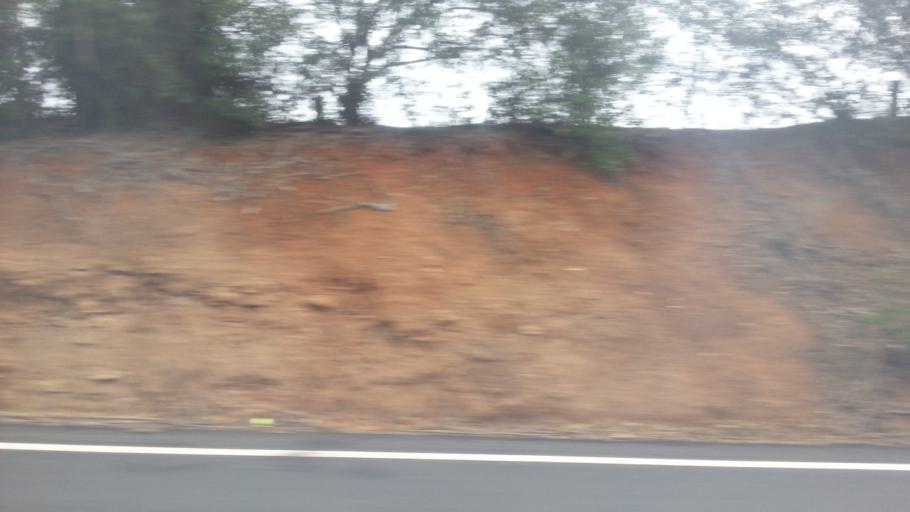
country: AU
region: New South Wales
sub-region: Camden
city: Camden South
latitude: -34.1303
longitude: 150.7051
